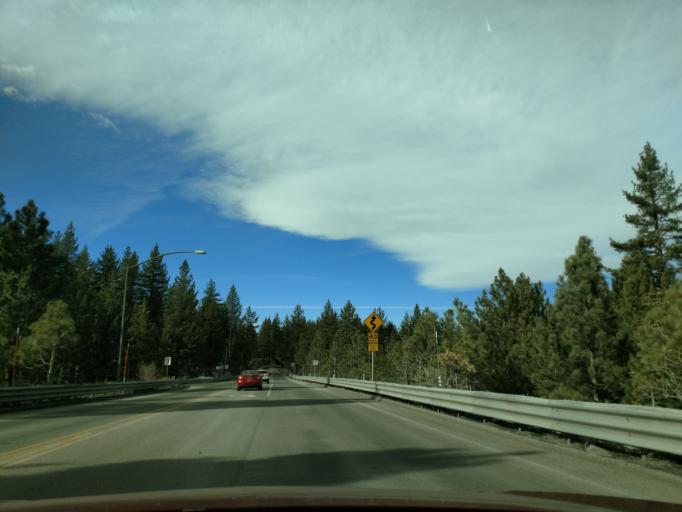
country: US
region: Nevada
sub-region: Douglas County
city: Kingsbury
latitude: 39.1021
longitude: -119.9121
